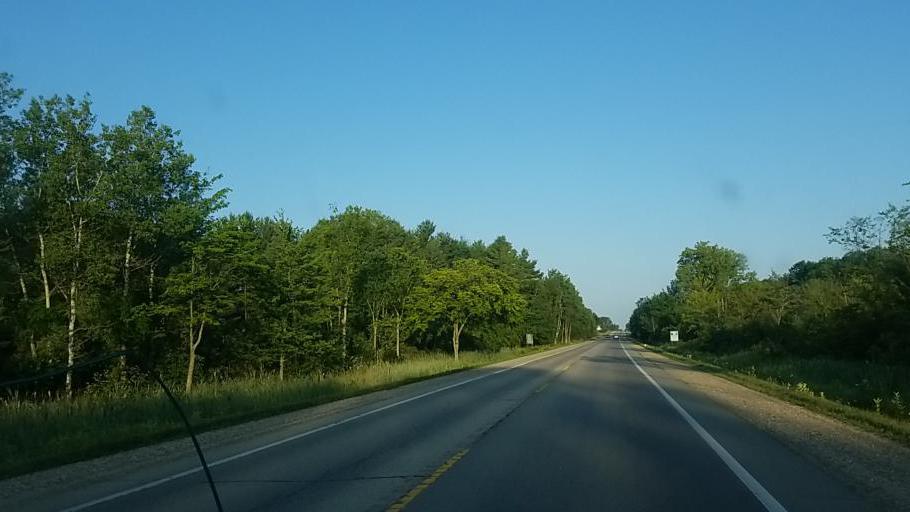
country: US
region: Michigan
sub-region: Montcalm County
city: Lakeview
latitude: 43.4309
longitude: -85.2220
